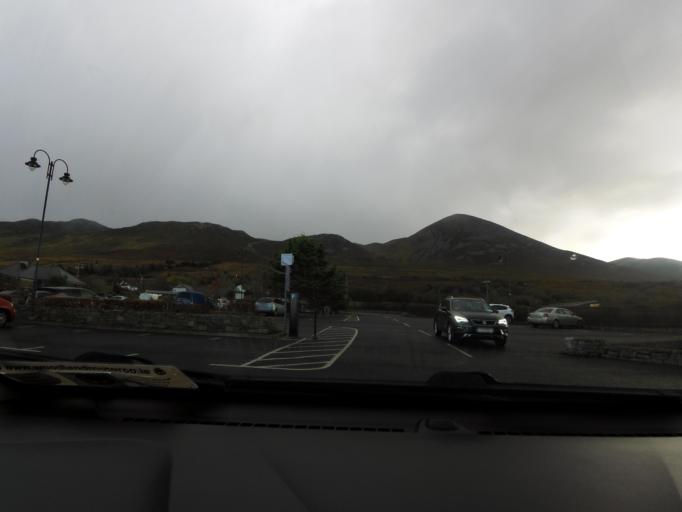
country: IE
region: Connaught
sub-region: Maigh Eo
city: Westport
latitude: 53.7795
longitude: -9.6403
